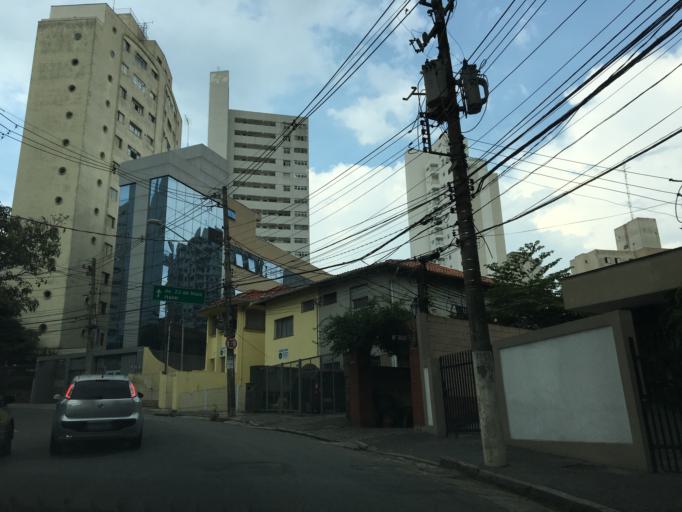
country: BR
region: Sao Paulo
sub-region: Sao Paulo
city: Sao Paulo
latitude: -23.5783
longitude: -46.6388
